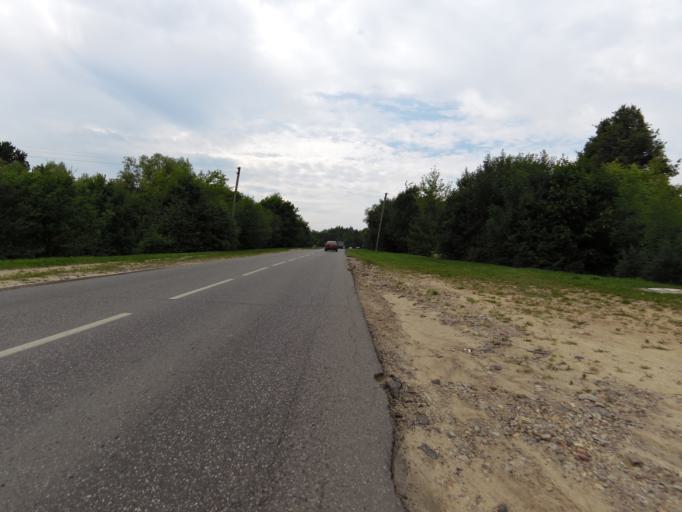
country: LT
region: Vilnius County
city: Seskine
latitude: 54.7229
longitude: 25.2752
